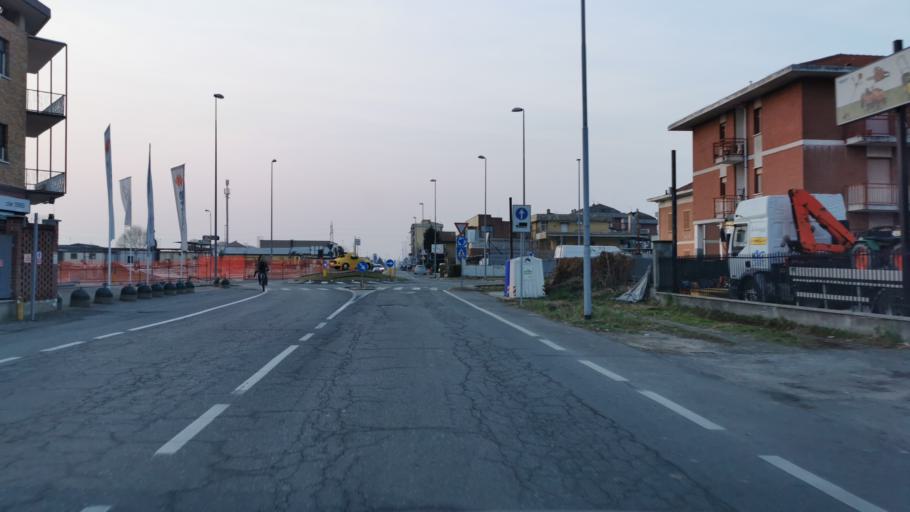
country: IT
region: Piedmont
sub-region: Provincia di Torino
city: Borgaro Torinese
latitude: 45.1493
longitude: 7.6550
